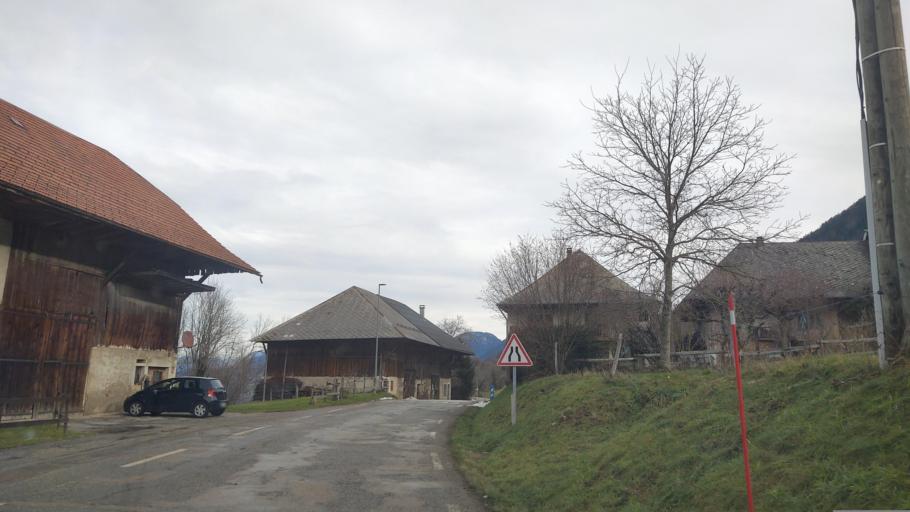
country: FR
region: Rhone-Alpes
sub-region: Departement de la Haute-Savoie
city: Cusy
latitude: 45.6826
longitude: 6.0658
